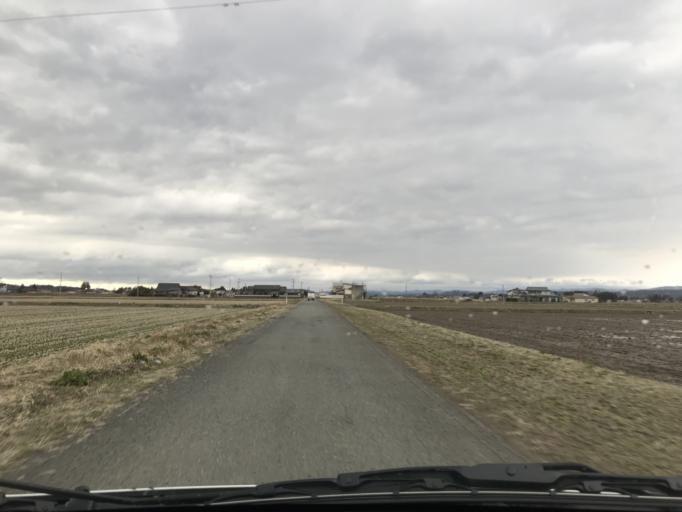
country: JP
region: Iwate
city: Mizusawa
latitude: 39.0790
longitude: 141.1564
